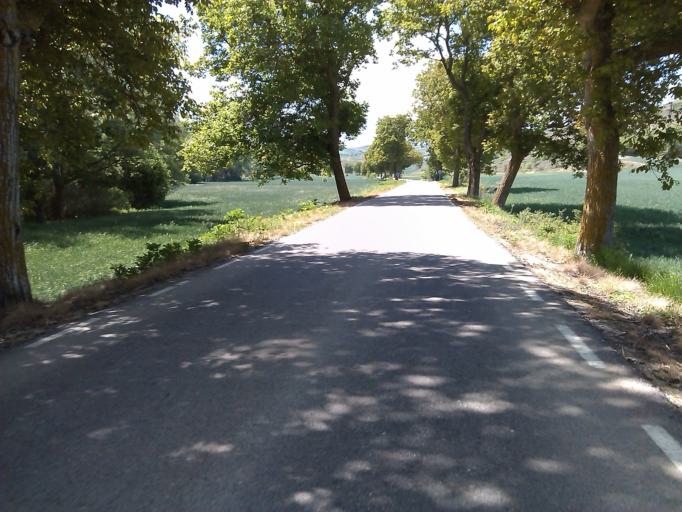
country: ES
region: Castille and Leon
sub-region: Provincia de Burgos
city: Alcocero de Mola
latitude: 42.4503
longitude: -3.3433
